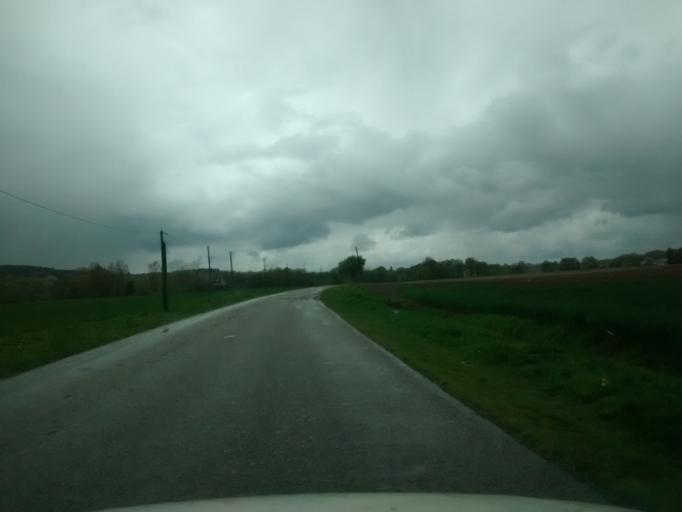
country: FR
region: Brittany
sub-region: Departement du Morbihan
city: Pleucadeuc
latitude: 47.7593
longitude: -2.3188
